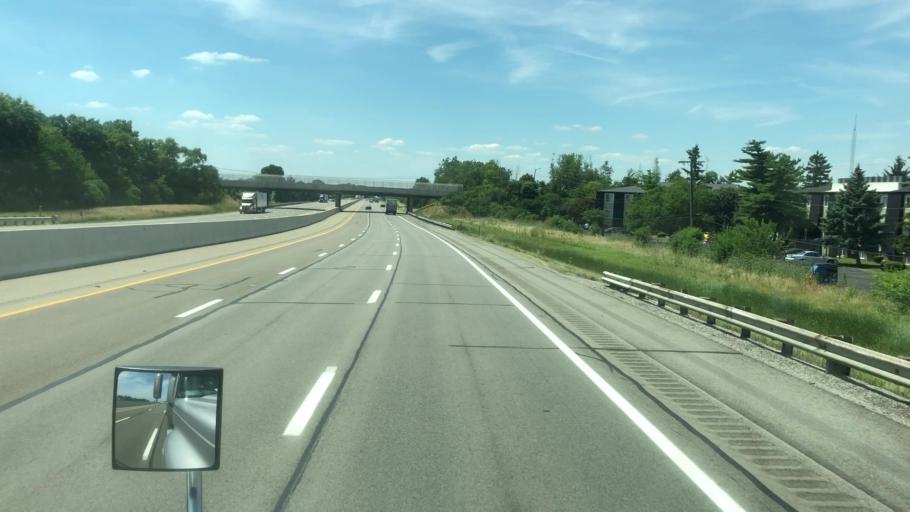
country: US
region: Ohio
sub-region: Lucas County
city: Maumee
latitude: 41.5908
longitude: -83.6429
